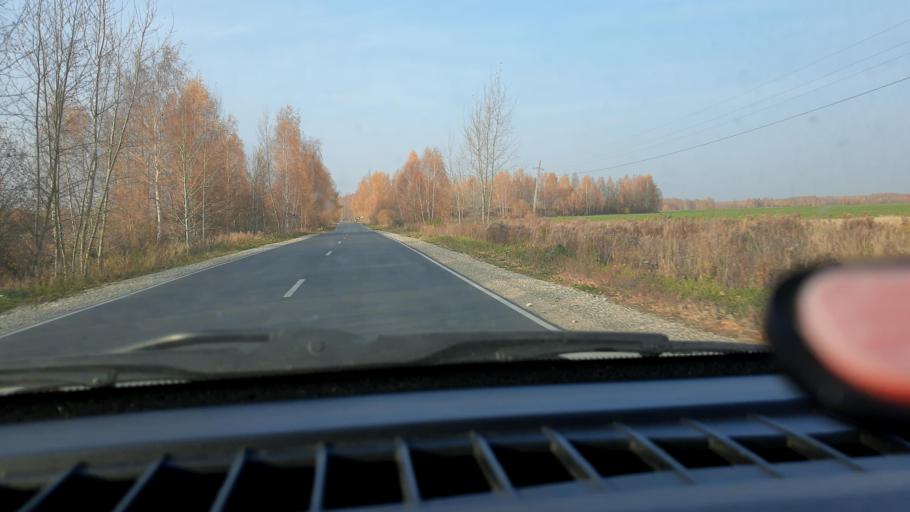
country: RU
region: Nizjnij Novgorod
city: Neklyudovo
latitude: 56.4607
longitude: 43.9023
